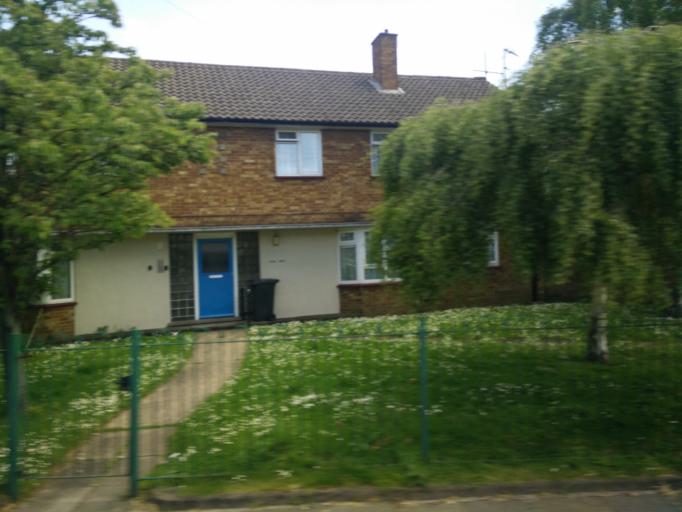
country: GB
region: England
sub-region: Luton
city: Luton
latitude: 51.8916
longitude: -0.4017
